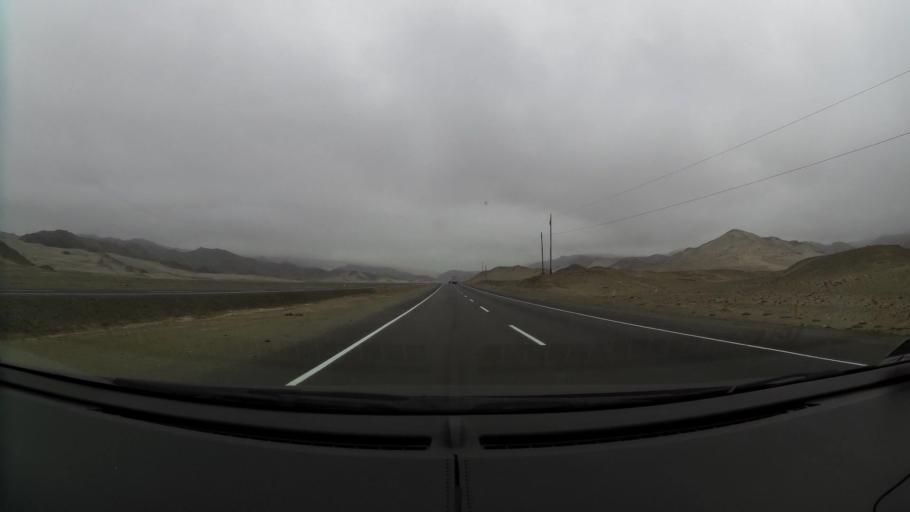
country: PE
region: La Libertad
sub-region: Viru
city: Chao
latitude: -8.7440
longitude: -78.6343
